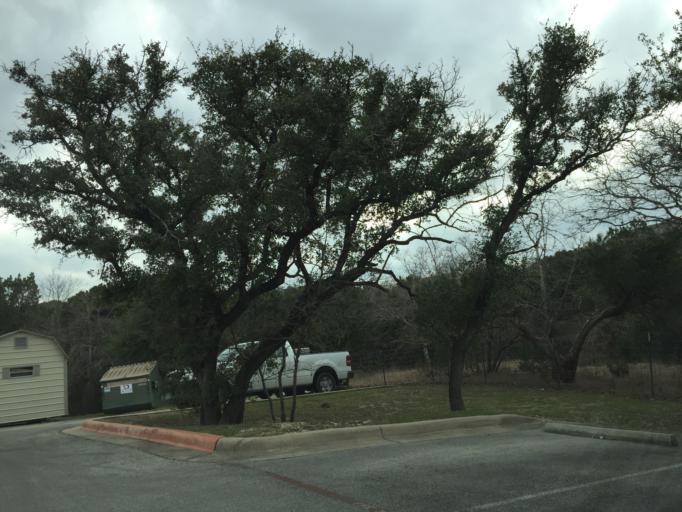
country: US
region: Texas
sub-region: Travis County
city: Wells Branch
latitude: 30.3894
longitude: -97.6748
